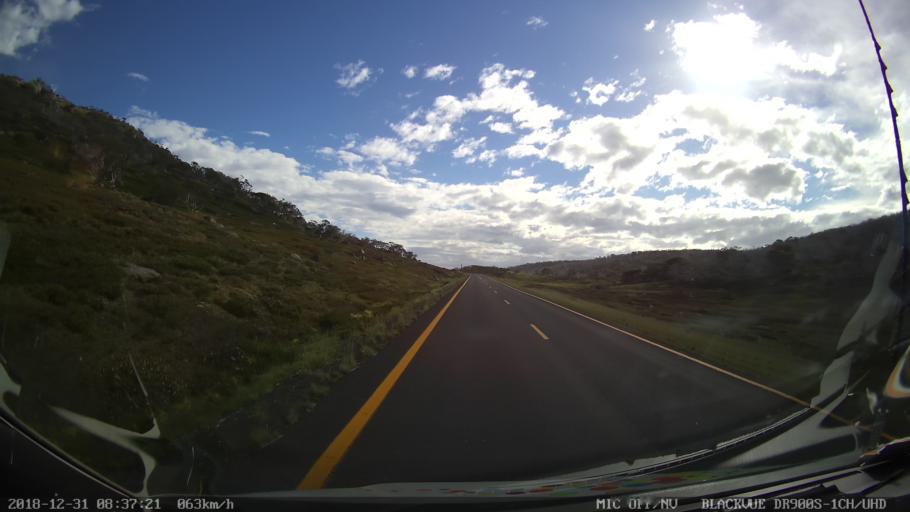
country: AU
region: New South Wales
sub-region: Snowy River
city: Jindabyne
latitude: -36.4198
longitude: 148.3844
